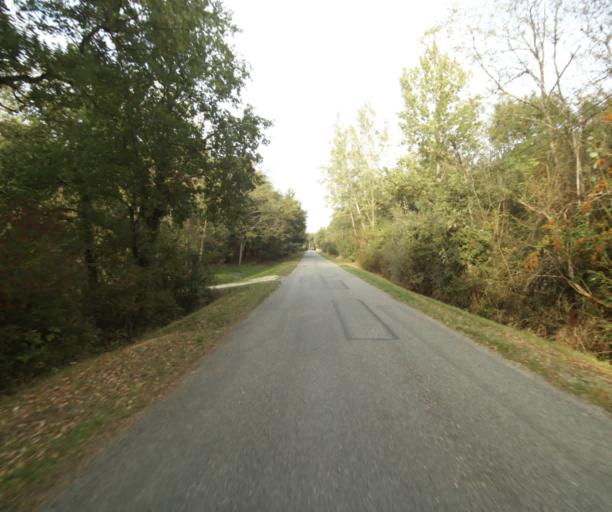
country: FR
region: Midi-Pyrenees
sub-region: Departement du Tarn-et-Garonne
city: Campsas
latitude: 43.8916
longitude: 1.3200
